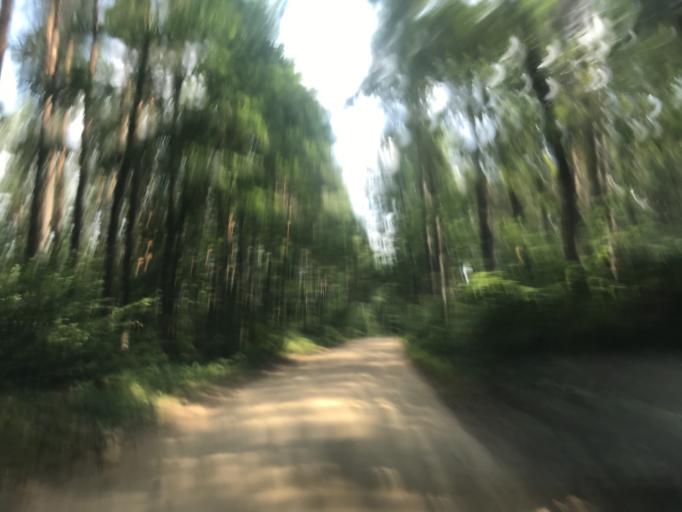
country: PL
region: Kujawsko-Pomorskie
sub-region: Powiat brodnicki
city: Brodnica
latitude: 53.3573
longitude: 19.4523
